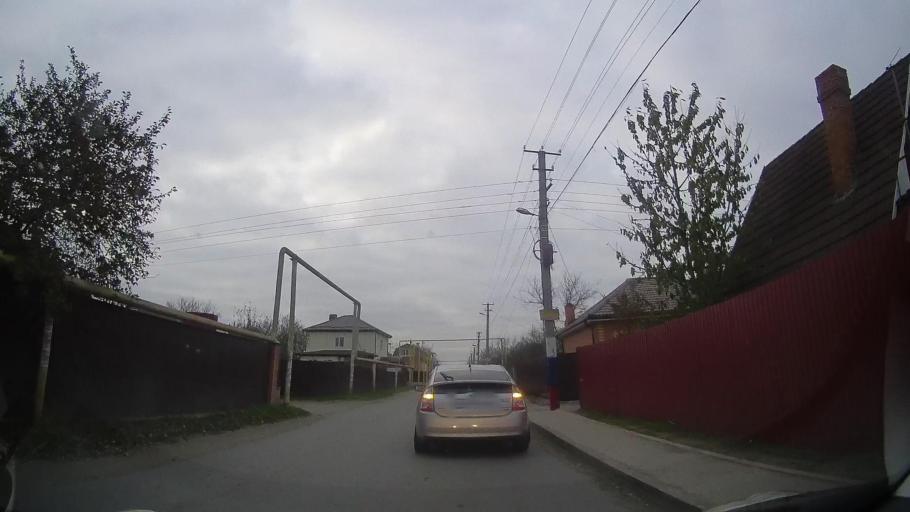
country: RU
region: Rostov
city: Bataysk
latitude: 47.0852
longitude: 39.7611
